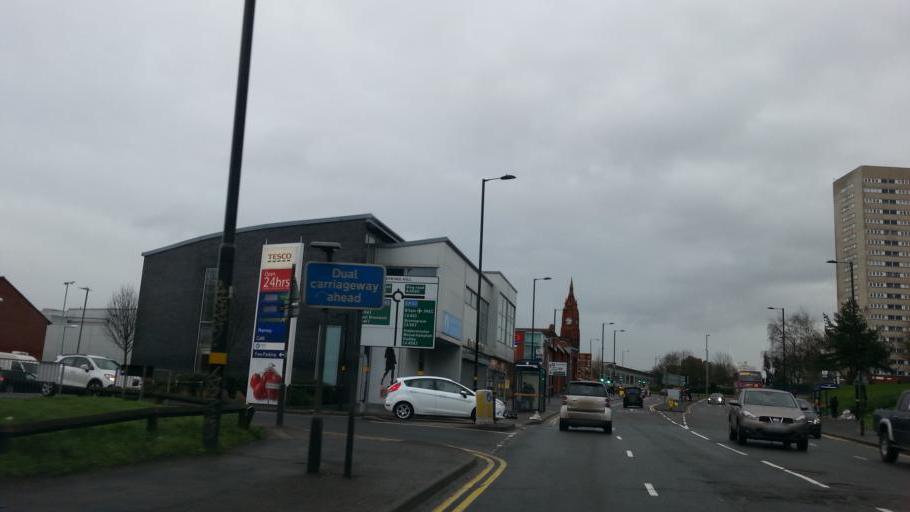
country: GB
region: England
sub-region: City and Borough of Birmingham
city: Hockley
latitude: 52.4856
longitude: -1.9220
